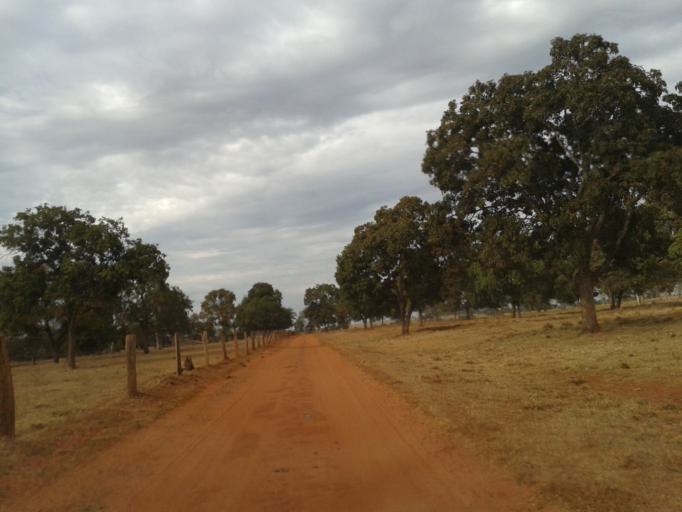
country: BR
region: Minas Gerais
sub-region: Santa Vitoria
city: Santa Vitoria
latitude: -18.7544
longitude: -50.1951
